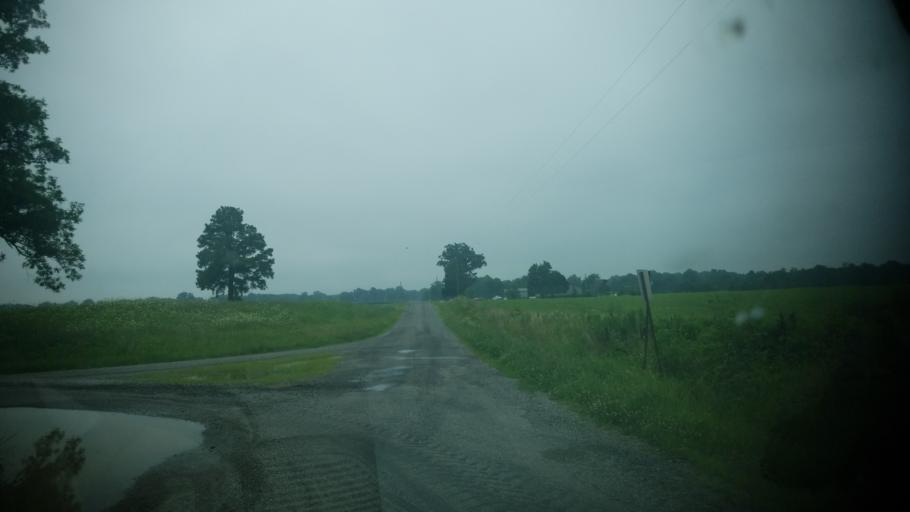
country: US
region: Illinois
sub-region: Clay County
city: Flora
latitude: 38.5879
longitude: -88.3646
